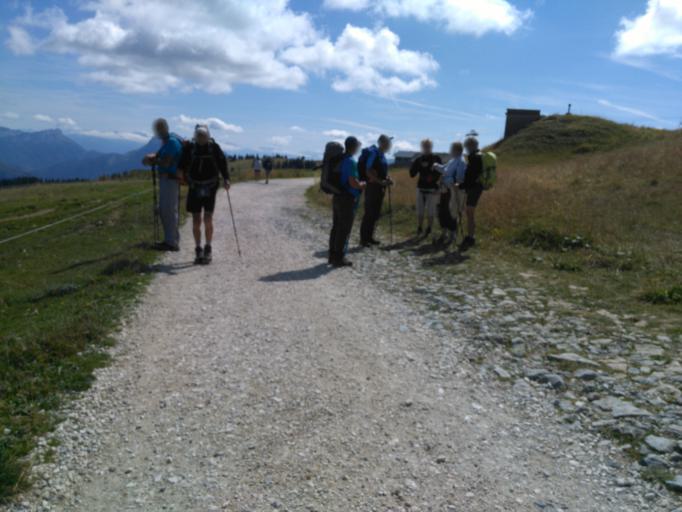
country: FR
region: Rhone-Alpes
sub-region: Departement de la Haute-Savoie
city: Viuz-la-Chiesaz
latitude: 45.7892
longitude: 6.0991
